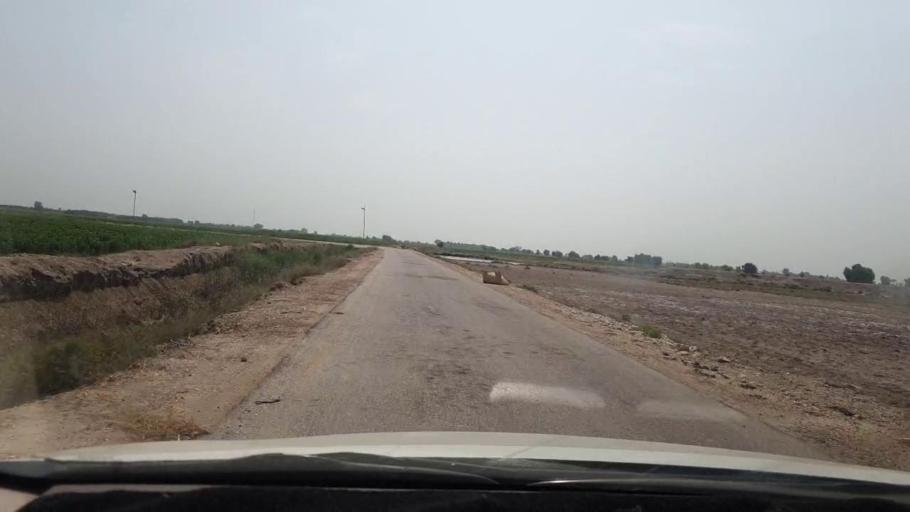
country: PK
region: Sindh
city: Rohri
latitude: 27.5381
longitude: 69.0096
